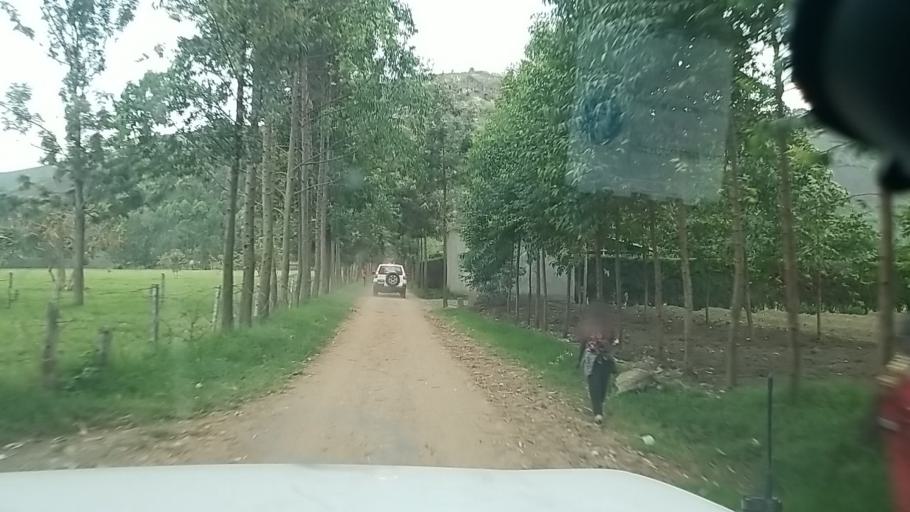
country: CD
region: Nord Kivu
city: Sake
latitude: -1.5651
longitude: 29.0439
